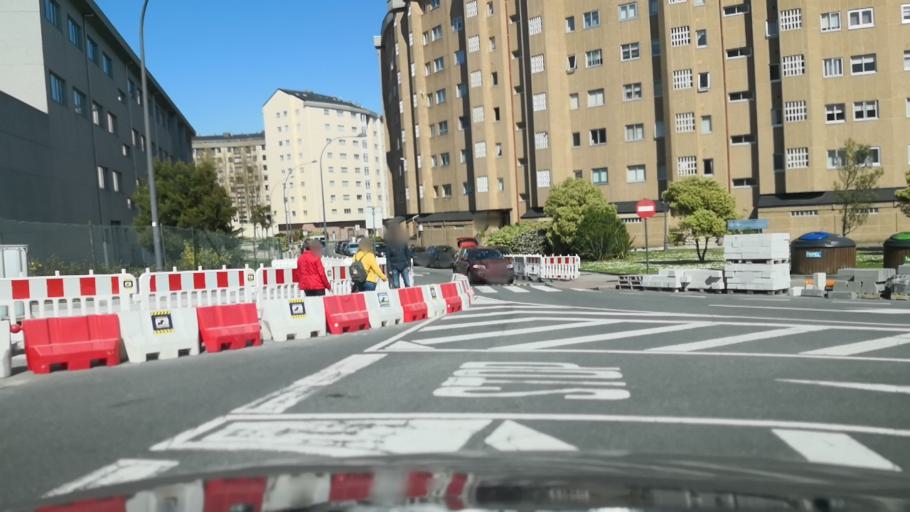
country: ES
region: Galicia
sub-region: Provincia da Coruna
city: A Coruna
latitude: 43.3824
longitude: -8.3967
